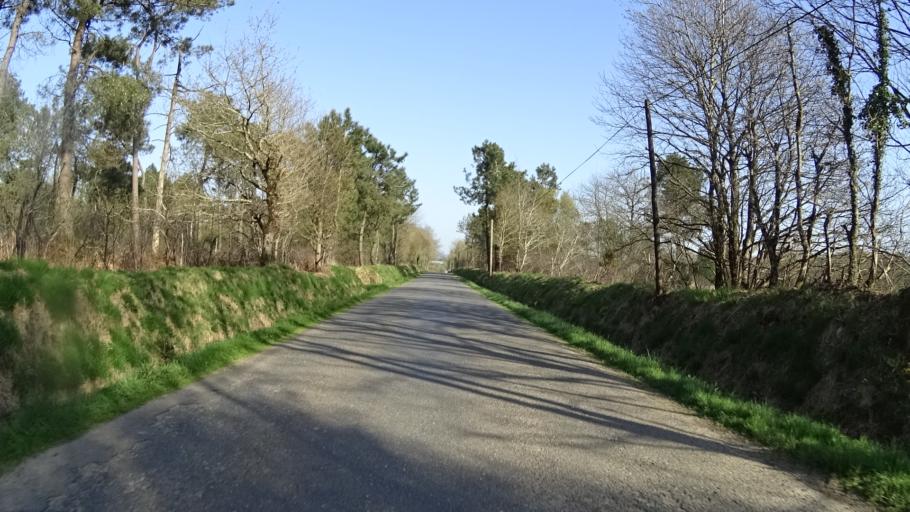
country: FR
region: Brittany
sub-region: Departement du Finistere
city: Hanvec
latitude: 48.3856
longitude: -4.1515
